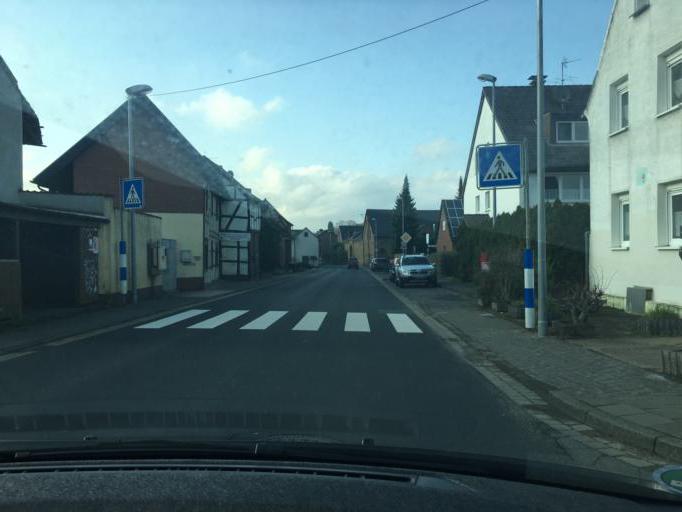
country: DE
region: North Rhine-Westphalia
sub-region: Regierungsbezirk Koln
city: Weilerswist
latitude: 50.7344
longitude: 6.8907
